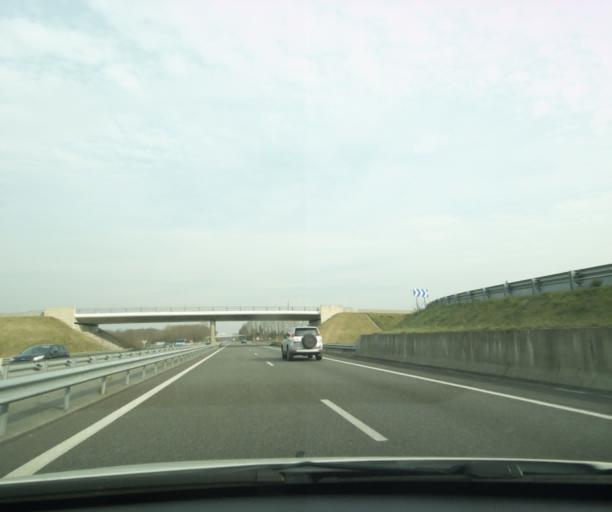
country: FR
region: Aquitaine
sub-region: Departement des Pyrenees-Atlantiques
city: Lescar
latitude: 43.3458
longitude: -0.4161
